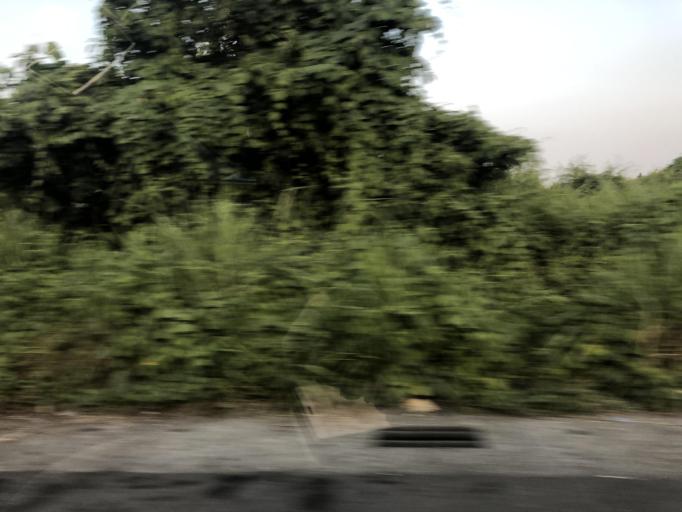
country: TW
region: Taiwan
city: Xinying
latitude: 23.1878
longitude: 120.2534
